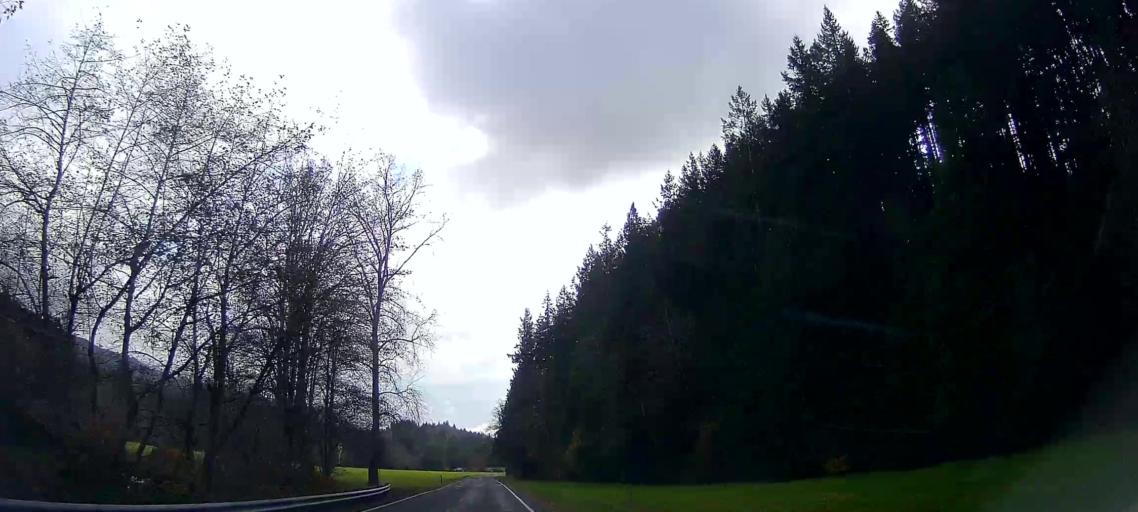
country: US
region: Washington
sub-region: Skagit County
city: Big Lake
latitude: 48.4185
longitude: -122.2086
